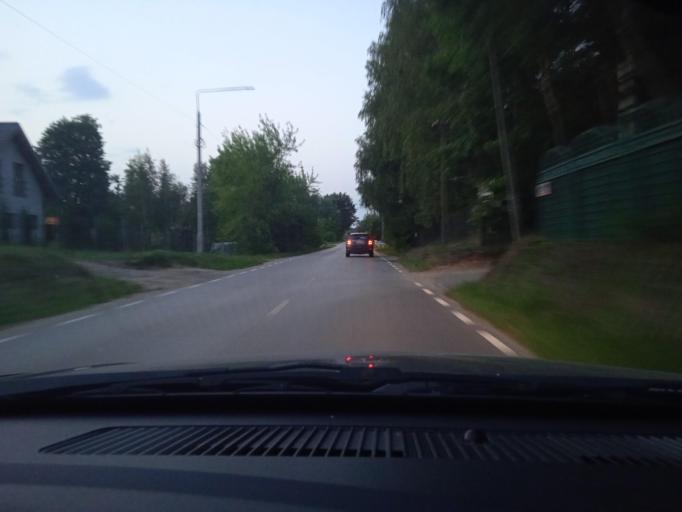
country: PL
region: Masovian Voivodeship
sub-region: Powiat nowodworski
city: Pomiechowek
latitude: 52.5164
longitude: 20.6794
